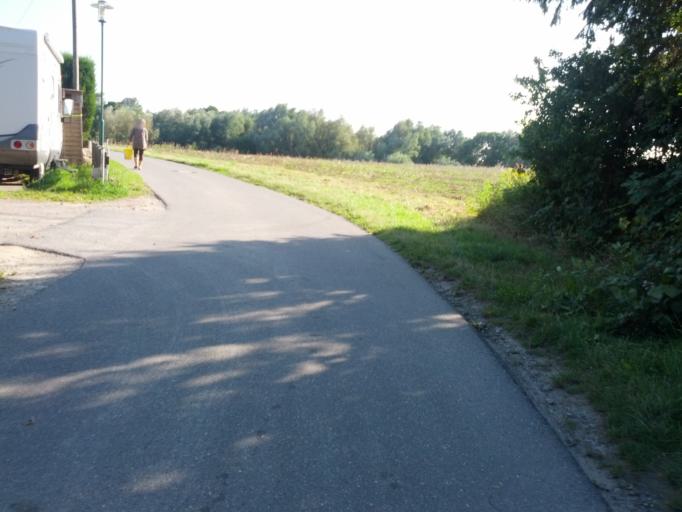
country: DE
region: Mecklenburg-Vorpommern
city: Bastorf
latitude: 54.1367
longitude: 11.6774
